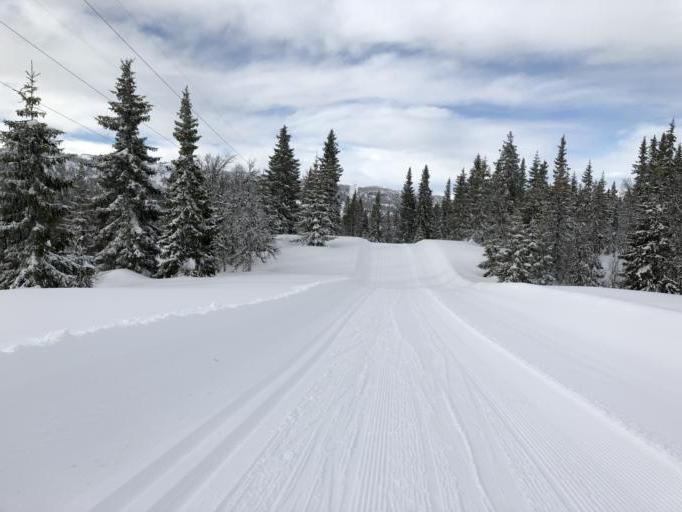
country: NO
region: Oppland
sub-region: Gausdal
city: Segalstad bru
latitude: 61.3231
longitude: 10.0801
